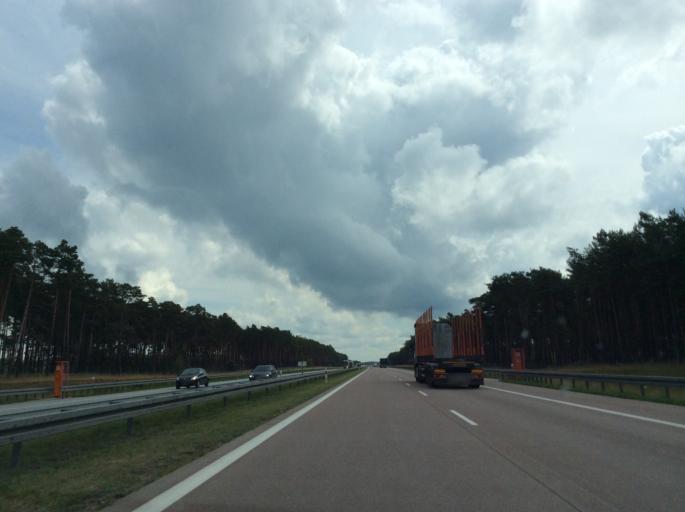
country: PL
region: Lubusz
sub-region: Powiat slubicki
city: Slubice
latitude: 52.3255
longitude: 14.6781
